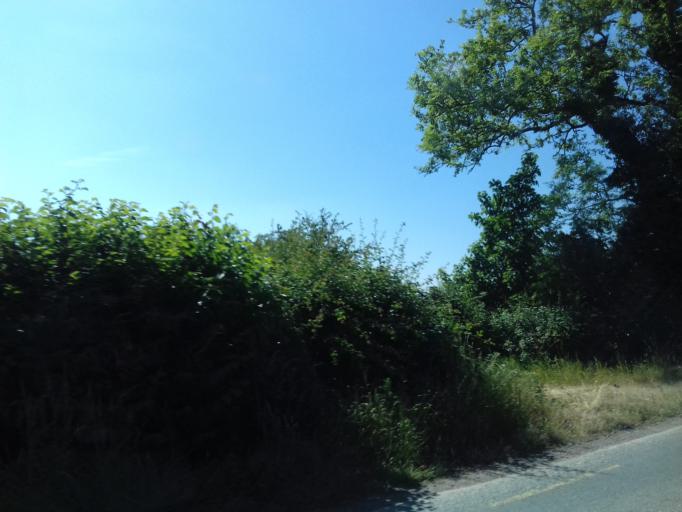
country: IE
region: Leinster
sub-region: An Mhi
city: Stamullin
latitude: 53.5681
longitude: -6.2796
